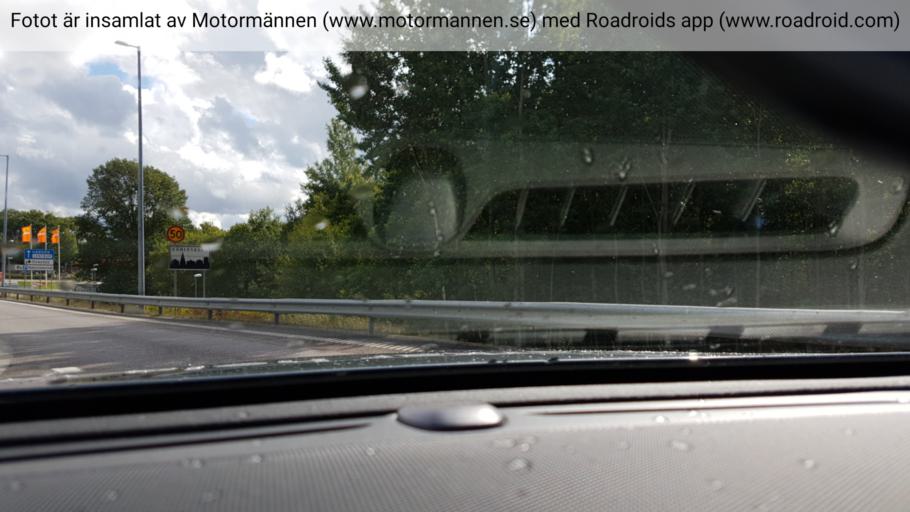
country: SE
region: Vaestra Goetaland
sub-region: Vanersborgs Kommun
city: Vanersborg
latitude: 58.3843
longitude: 12.3031
